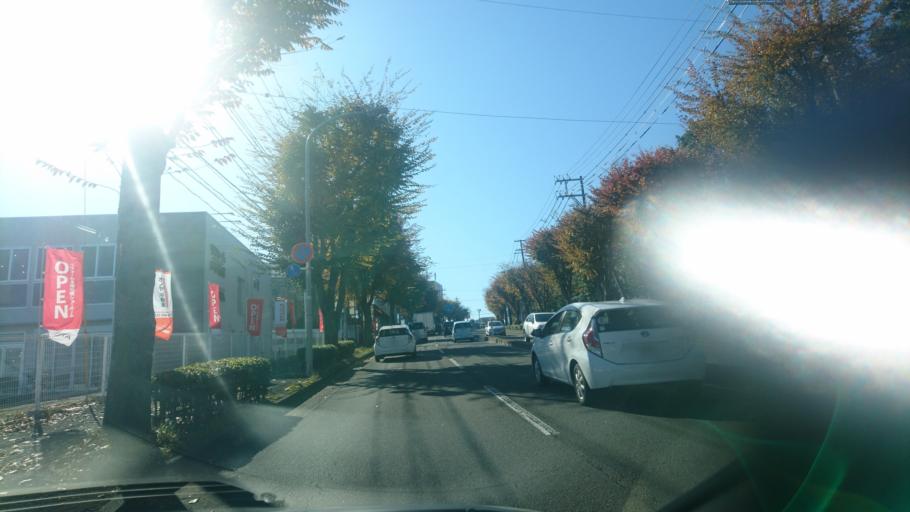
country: JP
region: Miyagi
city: Sendai-shi
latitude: 38.2990
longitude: 140.8294
